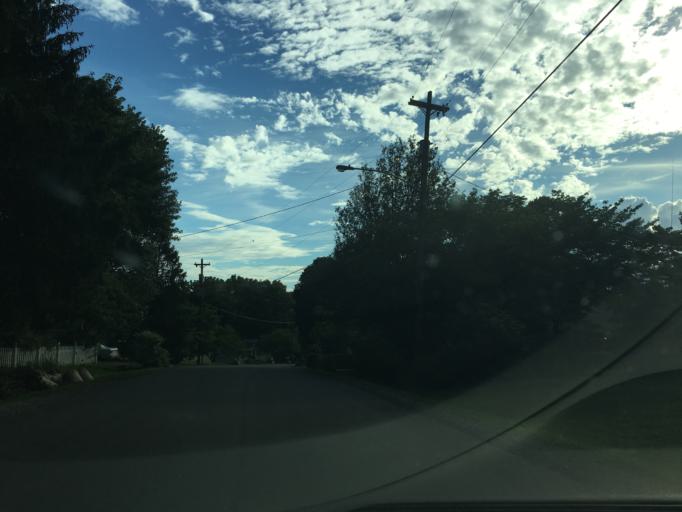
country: US
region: Tennessee
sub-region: Davidson County
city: Oak Hill
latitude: 36.0693
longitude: -86.7307
